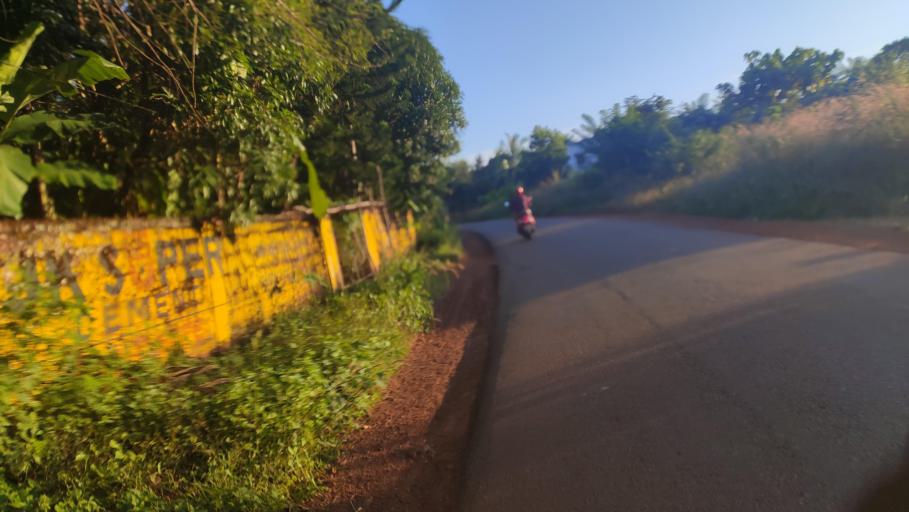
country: IN
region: Kerala
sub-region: Kasaragod District
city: Kannangad
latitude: 12.4140
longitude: 75.0950
